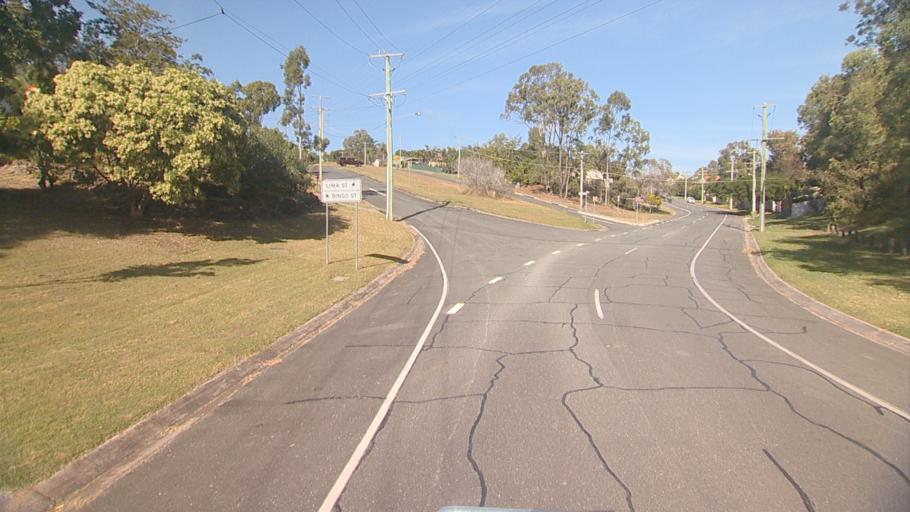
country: AU
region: Queensland
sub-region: Logan
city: Beenleigh
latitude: -27.7050
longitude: 153.1785
